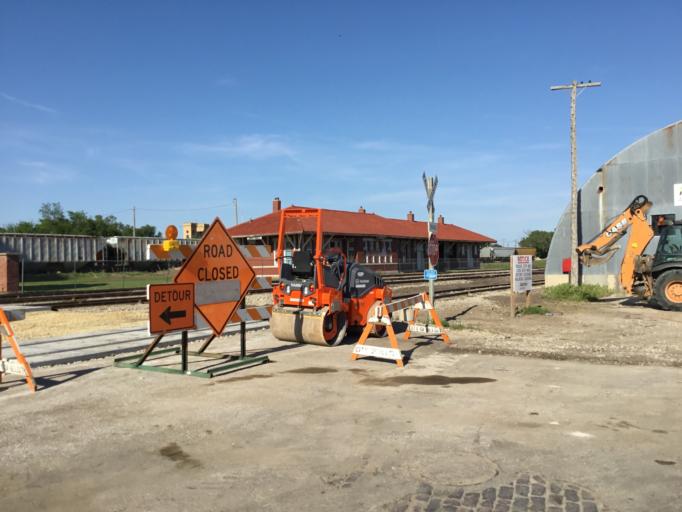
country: US
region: Kansas
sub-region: Mitchell County
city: Beloit
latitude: 39.4558
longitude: -98.1070
